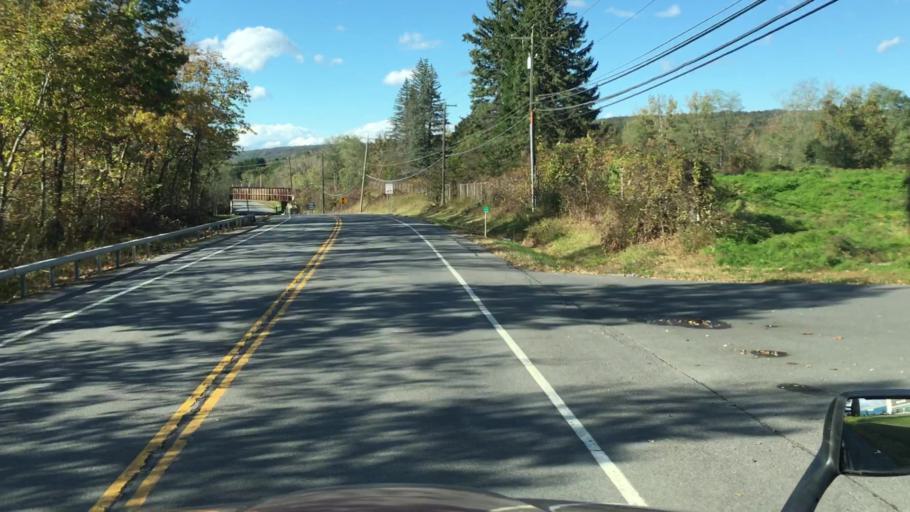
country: US
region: New York
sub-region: Schenectady County
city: Scotia
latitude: 42.8485
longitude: -74.0002
